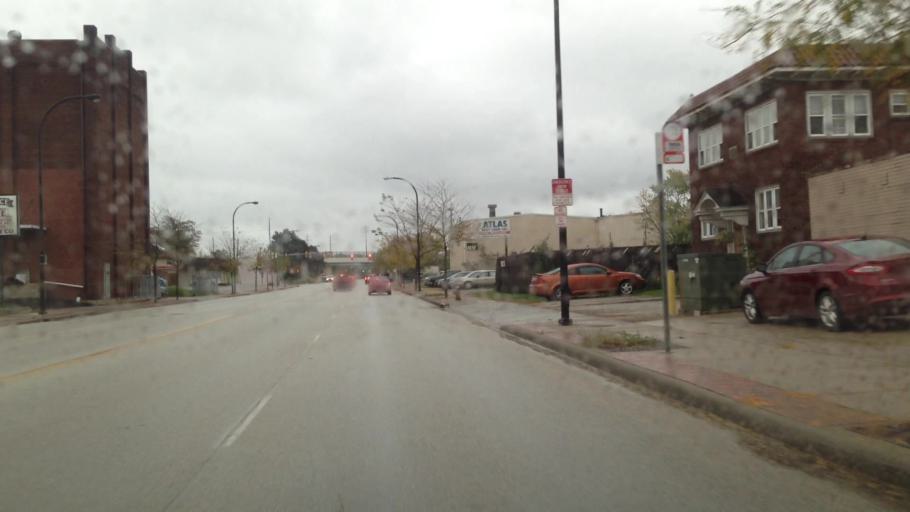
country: US
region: Ohio
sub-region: Summit County
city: Sawyerwood
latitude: 41.0625
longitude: -81.4701
